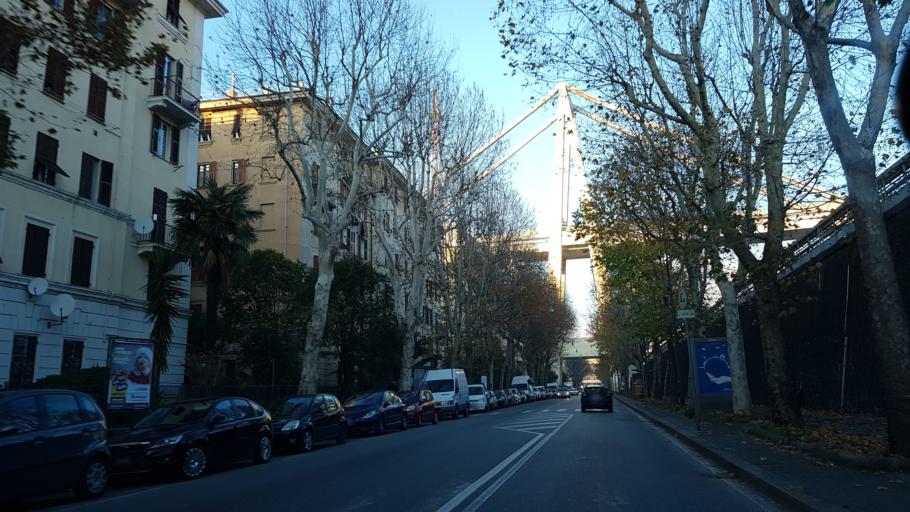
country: IT
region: Liguria
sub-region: Provincia di Genova
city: San Teodoro
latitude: 44.4234
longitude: 8.8896
